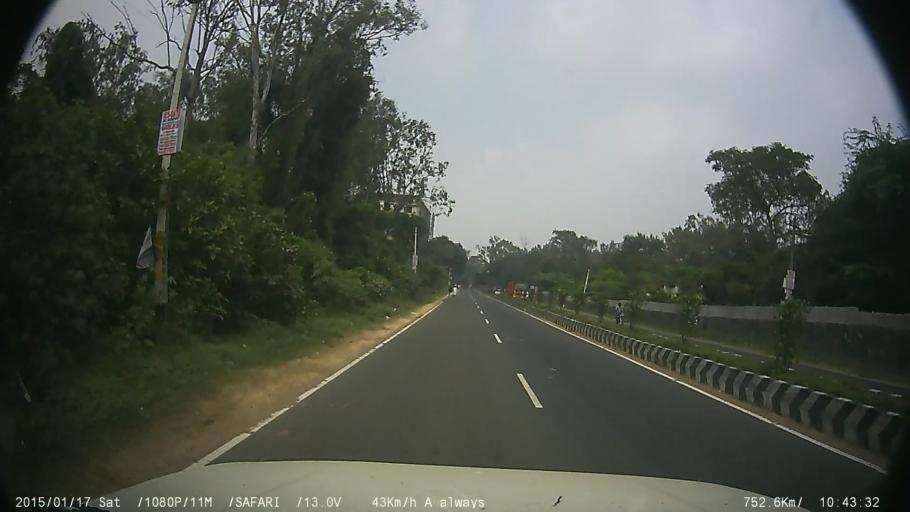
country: IN
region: Tamil Nadu
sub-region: Kancheepuram
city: Vandalur
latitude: 12.8757
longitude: 80.0878
